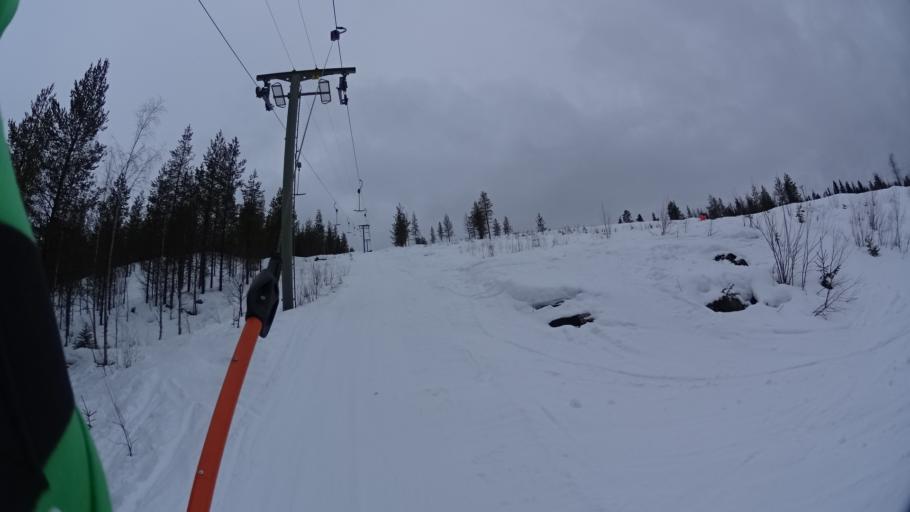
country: SE
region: Vaesterbotten
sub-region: Mala Kommun
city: Mala
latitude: 65.1803
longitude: 18.7694
